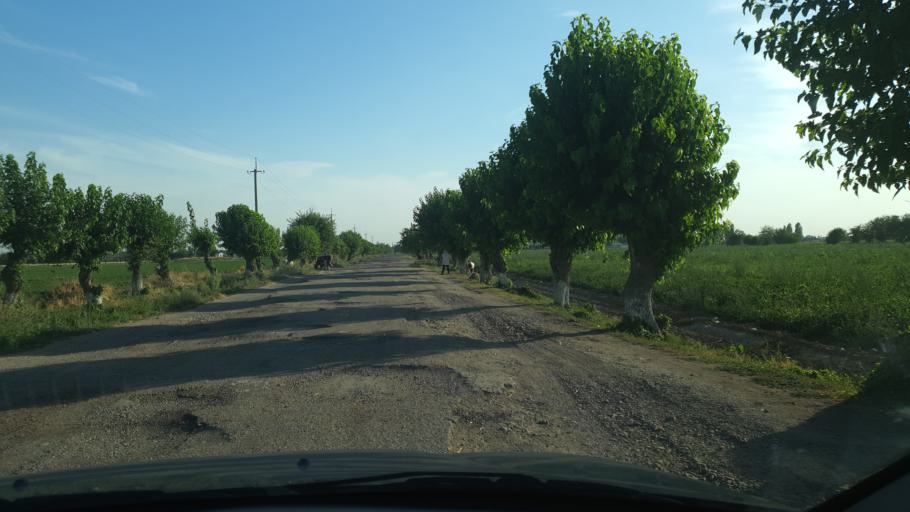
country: UZ
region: Toshkent
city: Tuytepa
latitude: 41.0938
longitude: 69.3713
